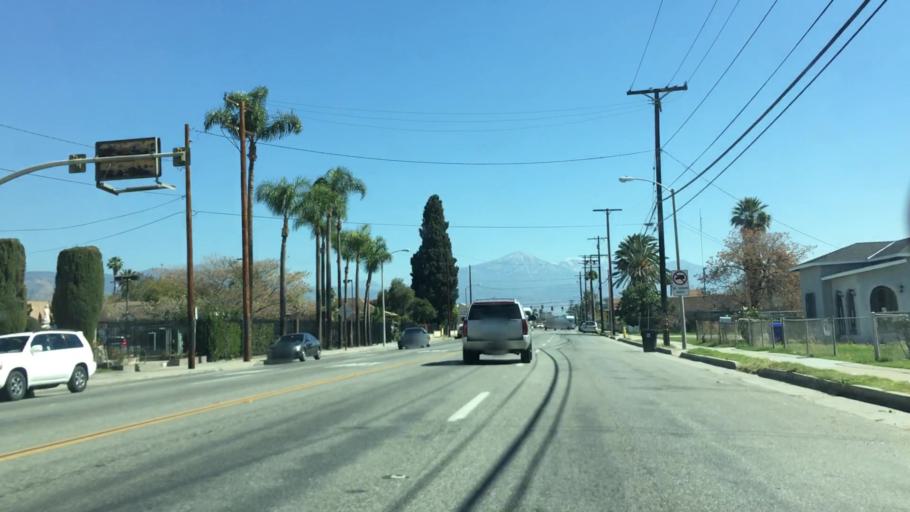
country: US
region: California
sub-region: San Bernardino County
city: San Bernardino
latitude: 34.1083
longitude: -117.3171
